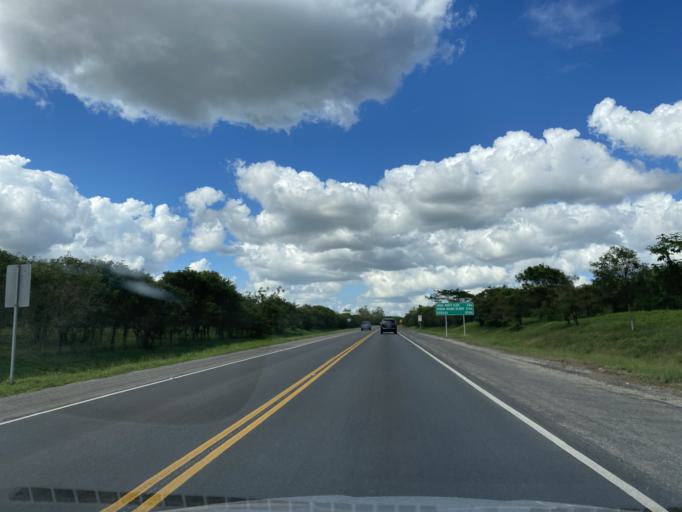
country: DO
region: Monte Plata
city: Monte Plata
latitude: 18.7160
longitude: -69.7579
